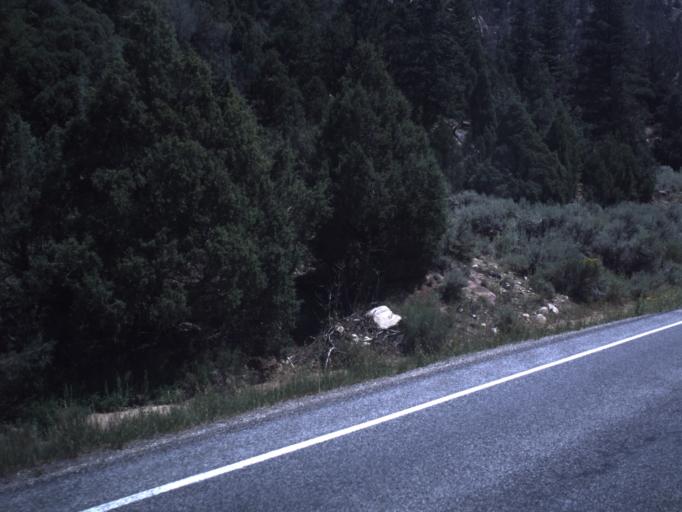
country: US
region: Utah
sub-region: Emery County
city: Huntington
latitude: 39.4363
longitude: -111.1324
